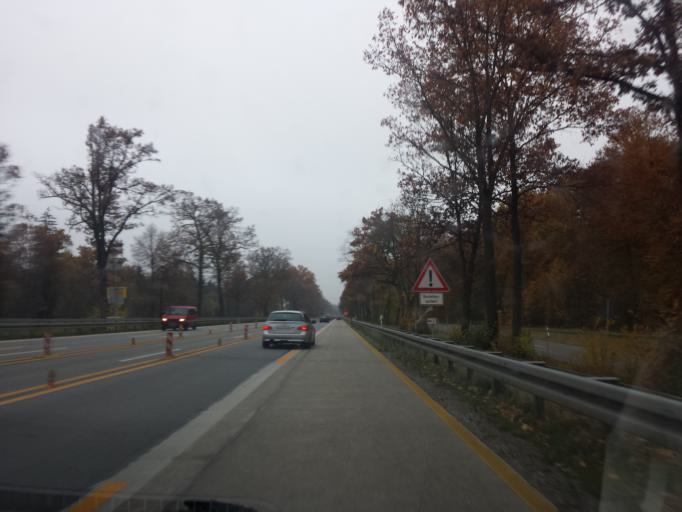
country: DE
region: Bavaria
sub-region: Upper Bavaria
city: Neuried
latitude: 48.0696
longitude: 11.4805
